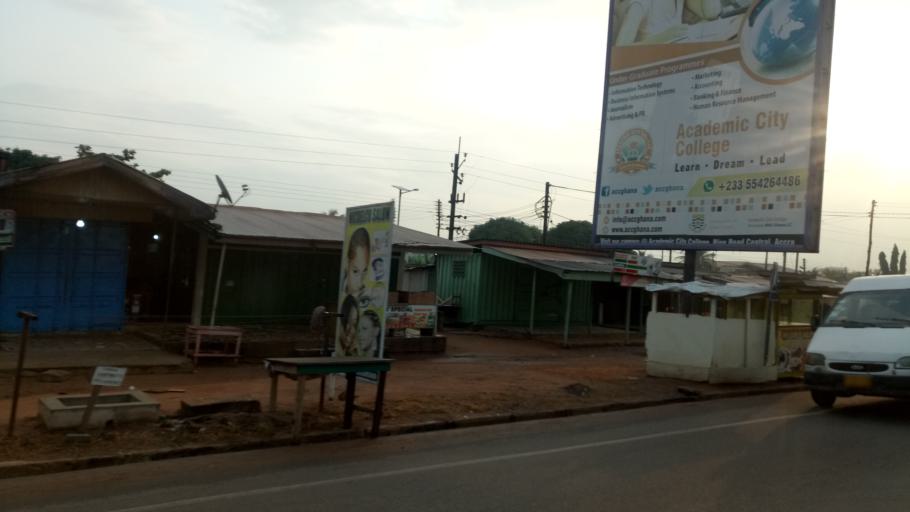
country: GH
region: Greater Accra
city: Medina Estates
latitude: 5.6672
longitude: -0.1826
